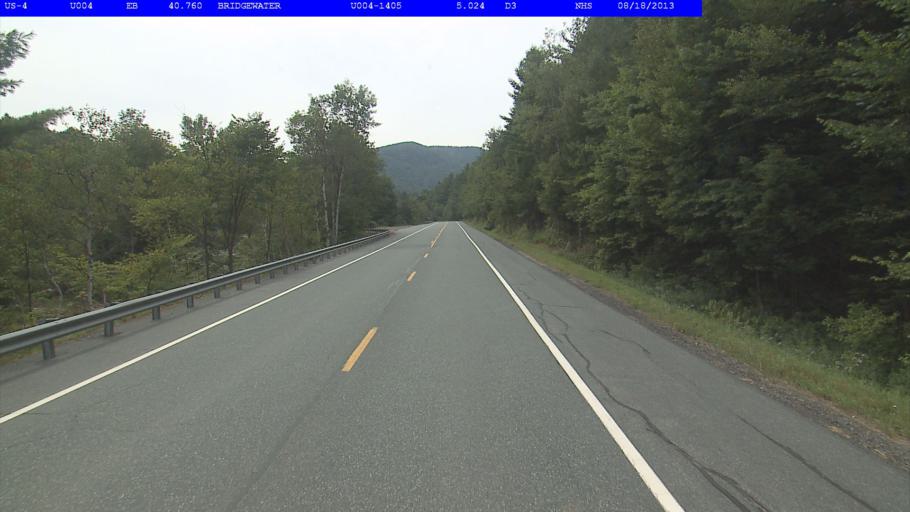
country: US
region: Vermont
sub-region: Windsor County
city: Woodstock
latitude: 43.5936
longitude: -72.6658
